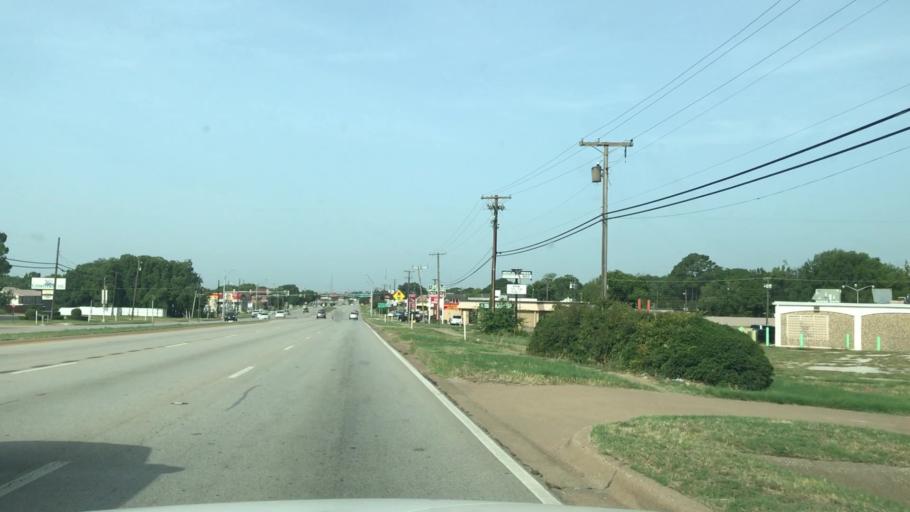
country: US
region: Texas
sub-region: Tarrant County
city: Euless
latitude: 32.8351
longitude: -97.0888
